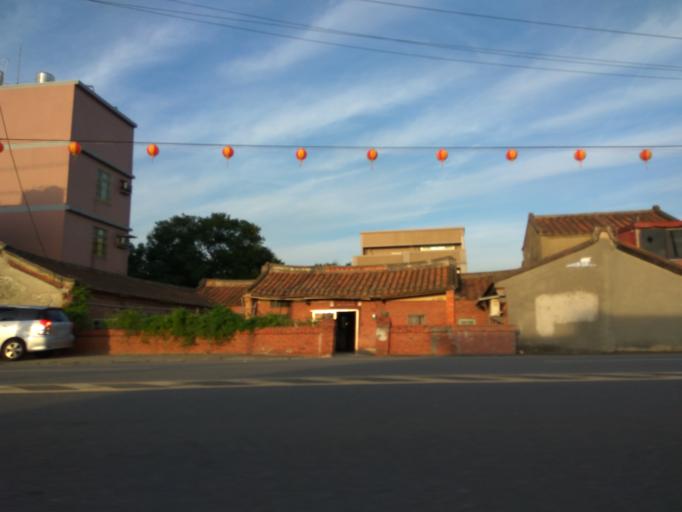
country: TW
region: Taiwan
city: Taoyuan City
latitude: 25.0031
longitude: 121.1524
